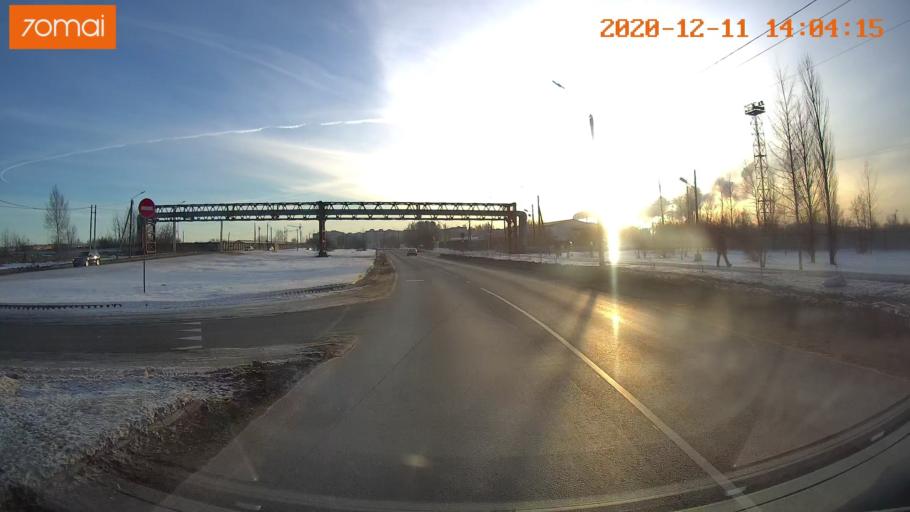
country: RU
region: Kostroma
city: Oktyabr'skiy
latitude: 57.7574
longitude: 41.0168
